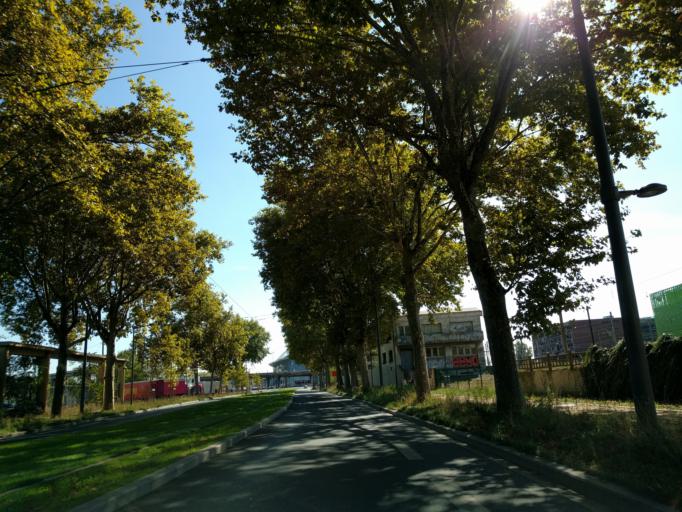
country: FR
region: Rhone-Alpes
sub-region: Departement du Rhone
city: La Mulatiere
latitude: 45.7364
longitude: 4.8167
